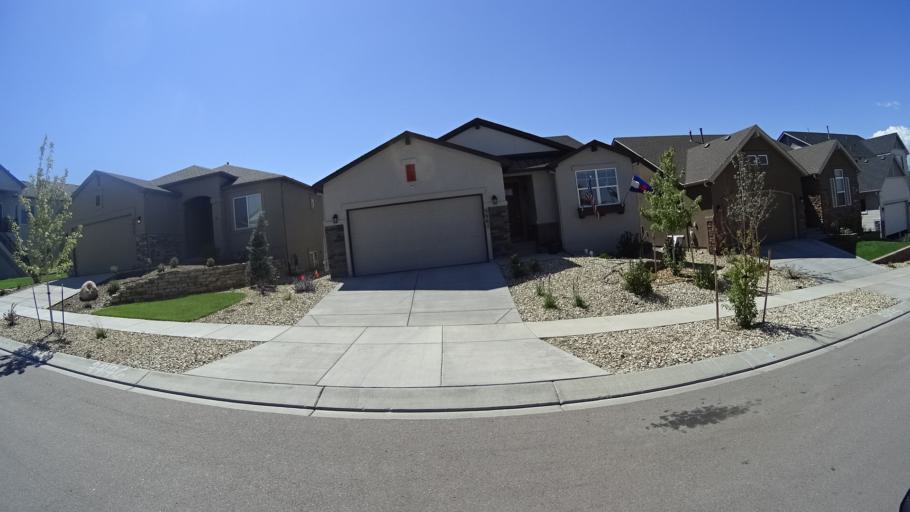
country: US
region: Colorado
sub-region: El Paso County
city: Black Forest
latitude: 38.9902
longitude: -104.7666
